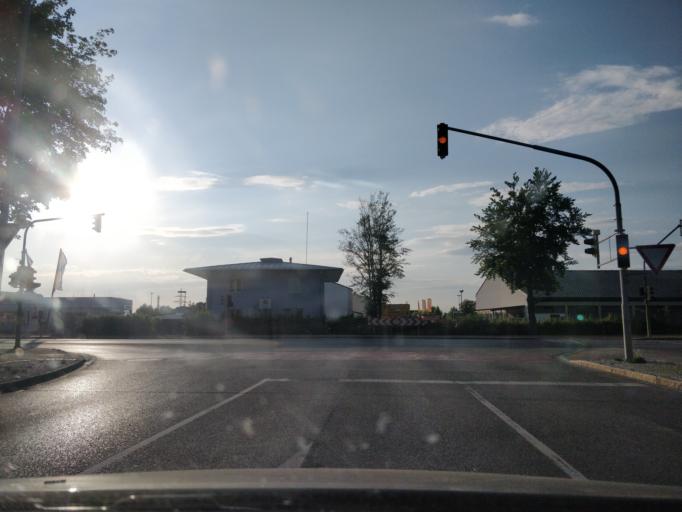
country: DE
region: Bavaria
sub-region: Swabia
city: Noerdlingen
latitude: 48.8607
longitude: 10.5031
